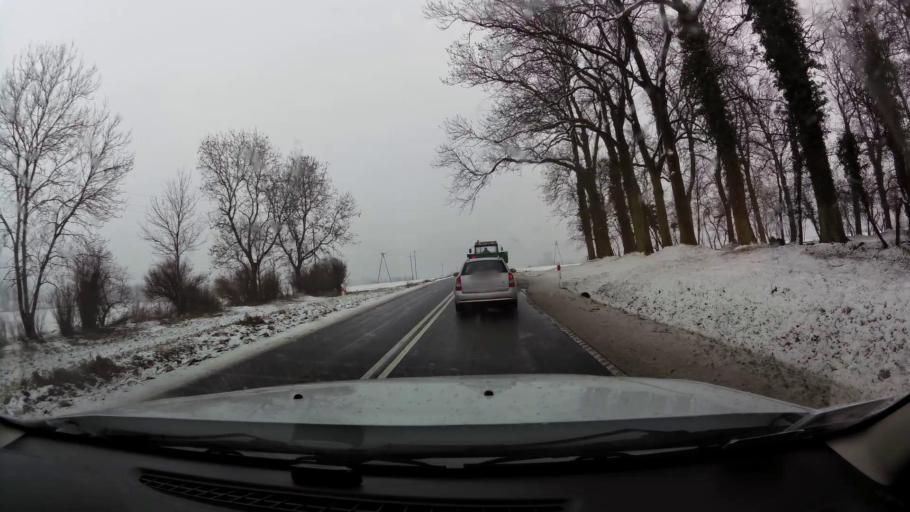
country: PL
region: West Pomeranian Voivodeship
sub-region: Powiat gryficki
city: Trzebiatow
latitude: 54.0825
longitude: 15.2565
